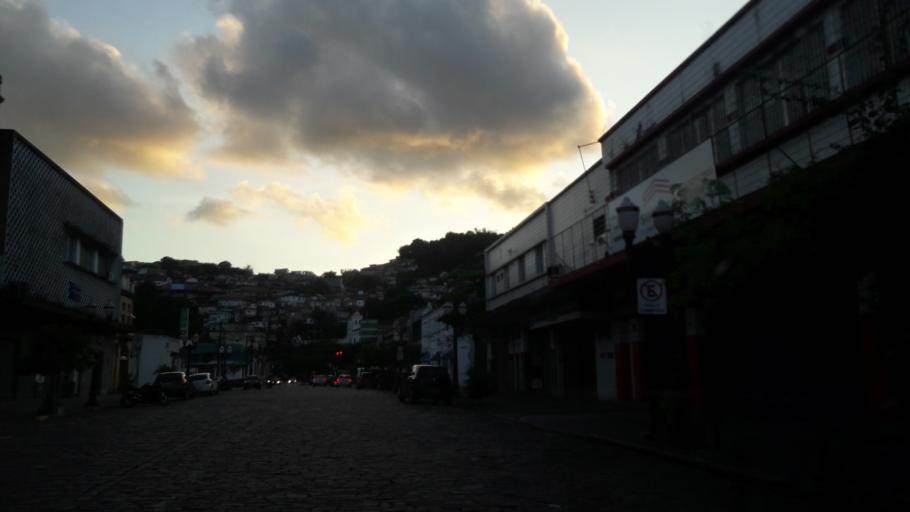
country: BR
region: Sao Paulo
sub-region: Santos
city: Santos
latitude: -23.9321
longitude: -46.3339
